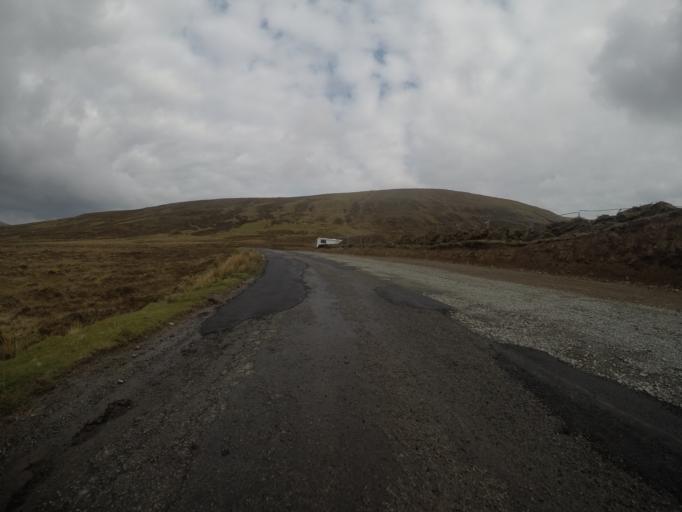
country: GB
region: Scotland
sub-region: Highland
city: Portree
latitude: 57.6268
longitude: -6.2941
